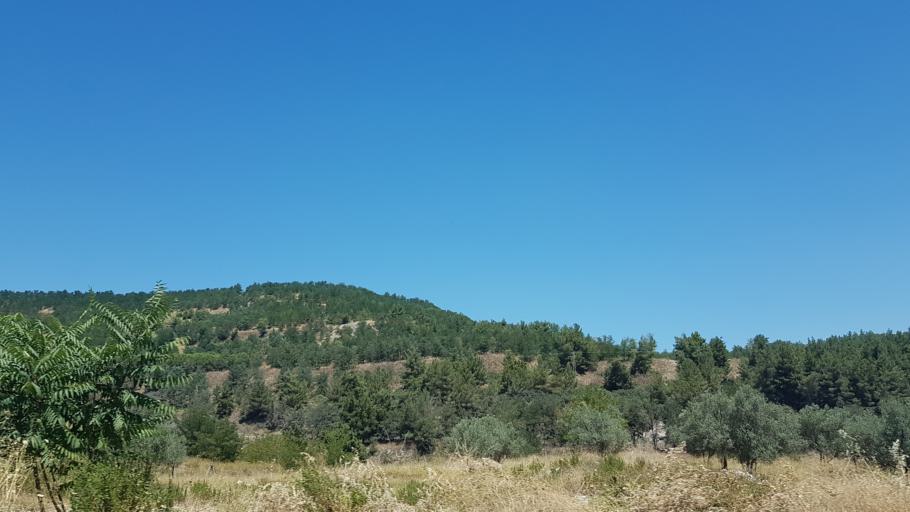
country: TR
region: Mugla
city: Yatagan
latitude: 37.3191
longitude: 28.0773
